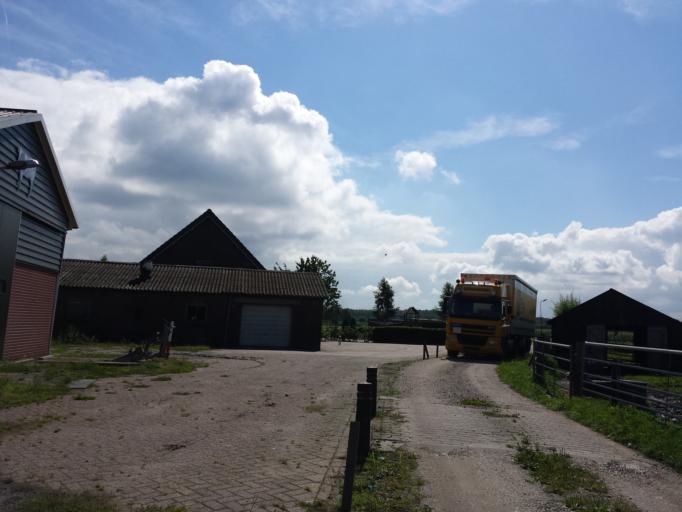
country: NL
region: Utrecht
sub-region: Gemeente Utrechtse Heuvelrug
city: Overberg
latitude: 52.0457
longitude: 5.5050
